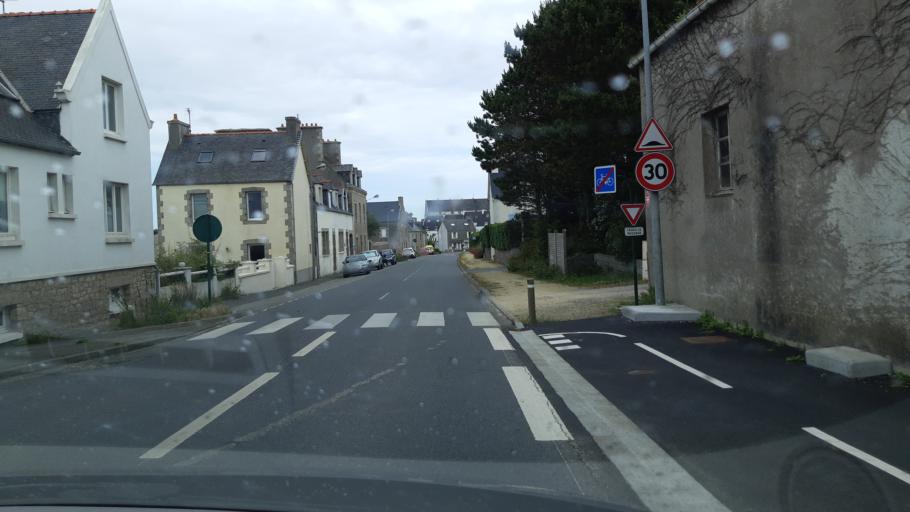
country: FR
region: Brittany
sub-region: Departement du Finistere
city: Roscoff
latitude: 48.7146
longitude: -3.9845
